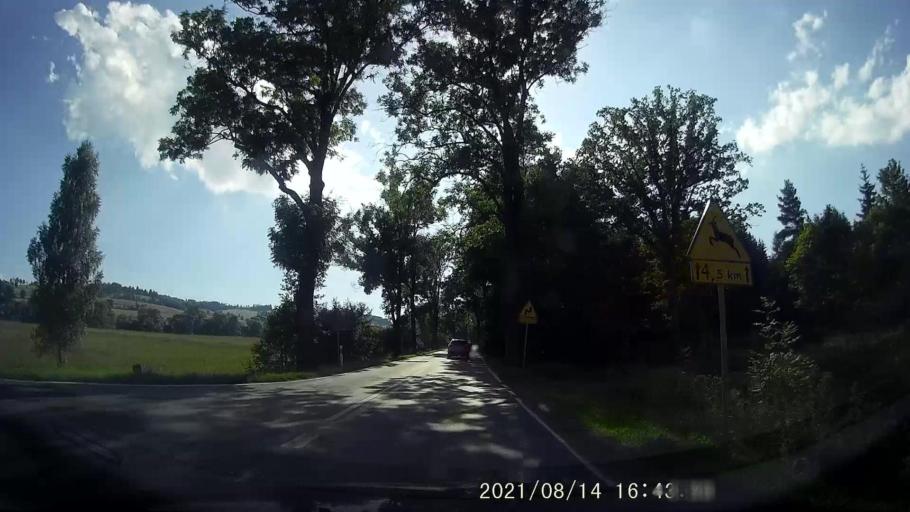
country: PL
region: Lower Silesian Voivodeship
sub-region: Powiat kamiennogorski
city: Kamienna Gora
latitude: 50.7757
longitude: 15.9892
